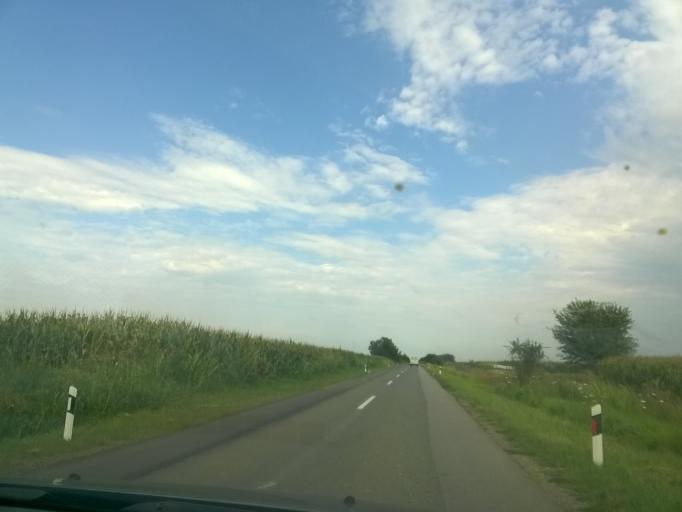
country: RS
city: Orlovat
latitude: 45.2624
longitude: 20.5500
